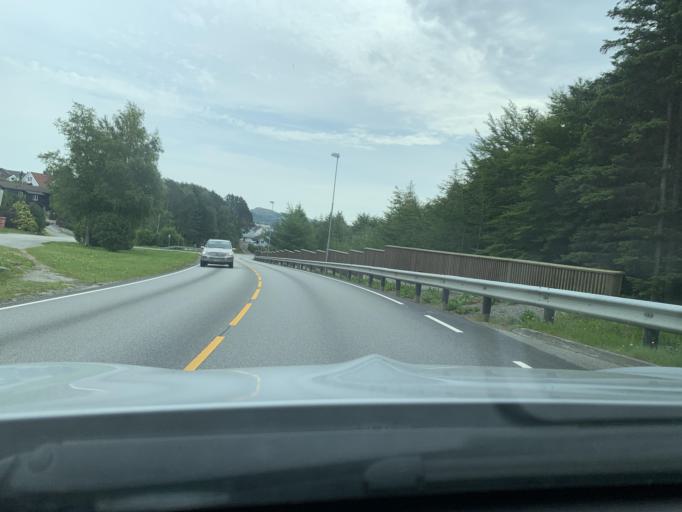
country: NO
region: Rogaland
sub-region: Sandnes
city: Sandnes
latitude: 58.7841
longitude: 5.7096
